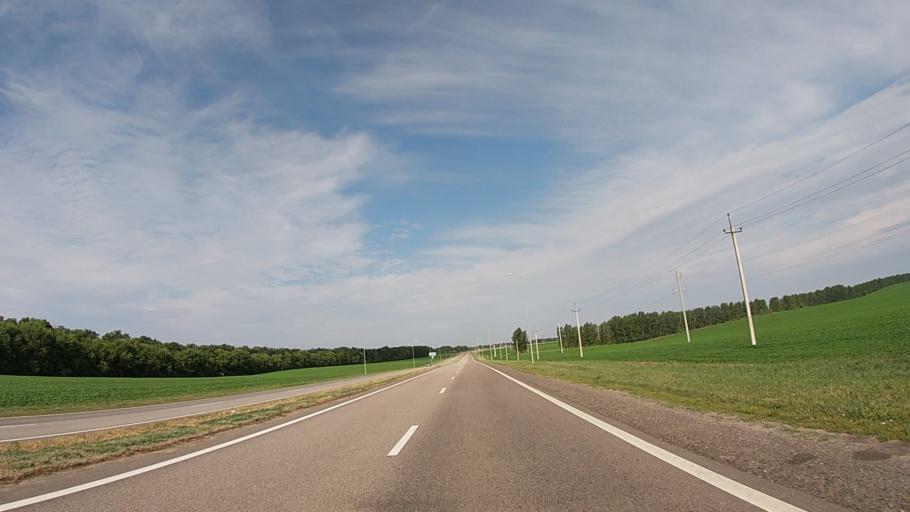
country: RU
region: Belgorod
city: Rakitnoye
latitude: 50.7904
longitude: 35.8820
